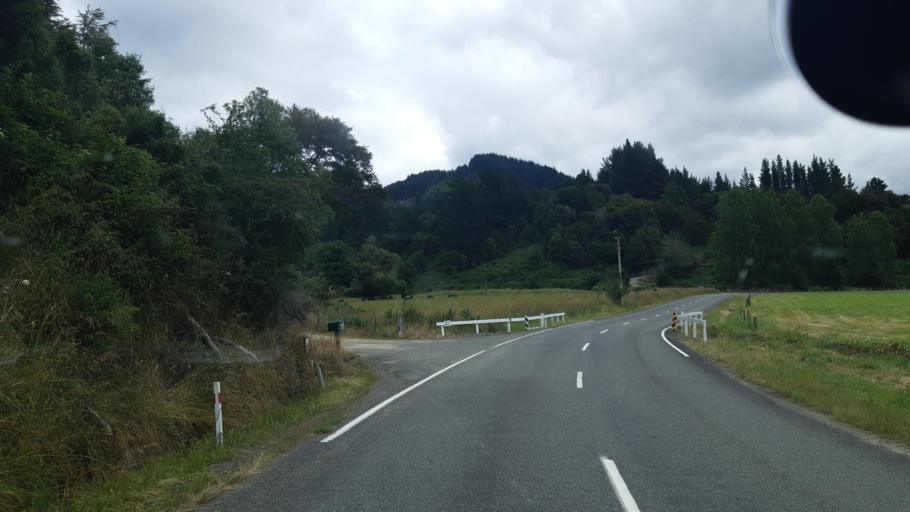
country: NZ
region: Marlborough
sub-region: Marlborough District
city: Blenheim
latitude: -41.4744
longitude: 173.7384
